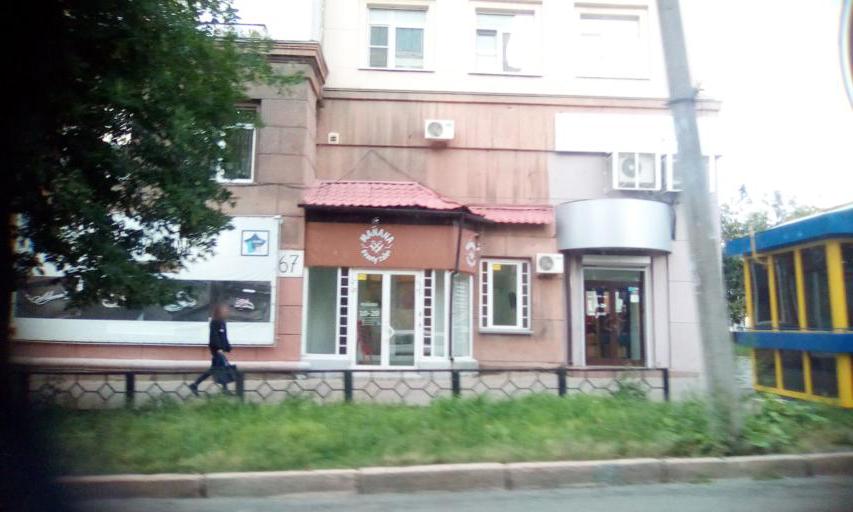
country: RU
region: Chelyabinsk
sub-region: Gorod Chelyabinsk
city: Chelyabinsk
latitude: 55.1610
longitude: 61.4068
